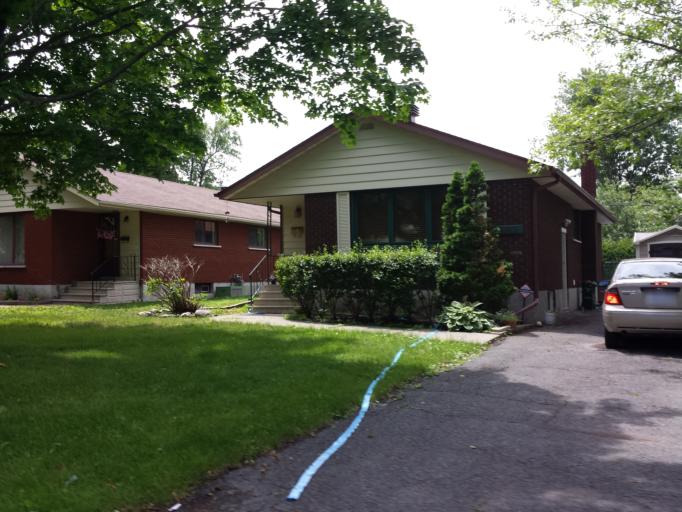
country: CA
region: Ontario
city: Bells Corners
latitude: 45.3512
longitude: -75.7773
